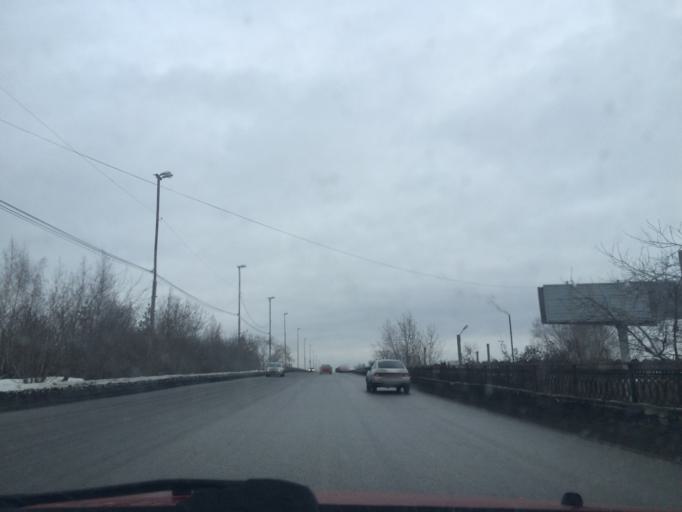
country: RU
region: Sverdlovsk
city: Yekaterinburg
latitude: 56.8645
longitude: 60.6687
